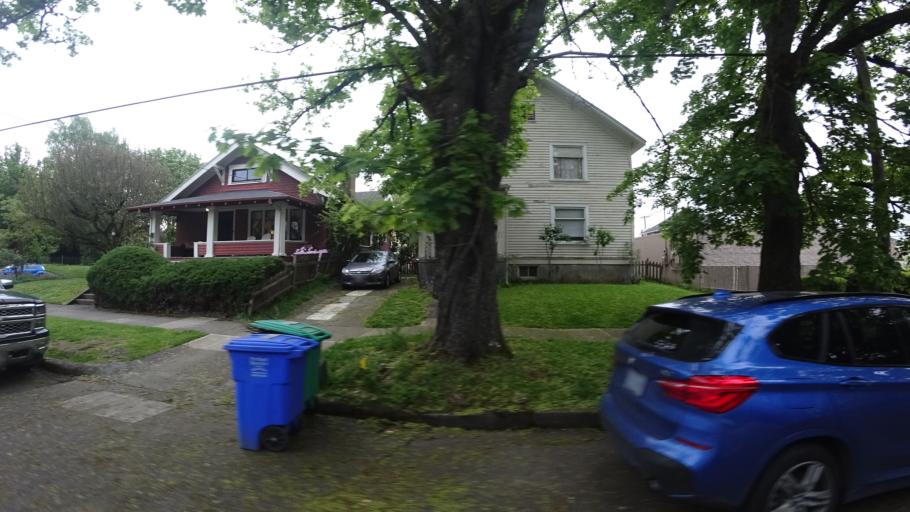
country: US
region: Oregon
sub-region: Clackamas County
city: Milwaukie
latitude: 45.4751
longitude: -122.6497
